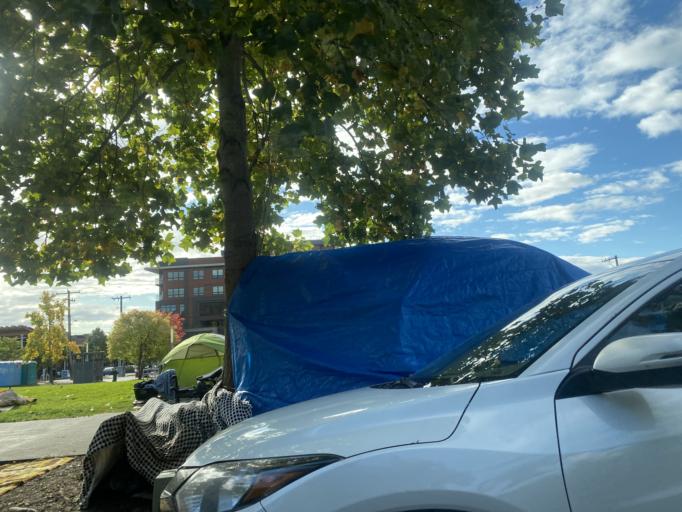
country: US
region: Washington
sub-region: King County
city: Seattle
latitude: 47.6709
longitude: -122.3852
